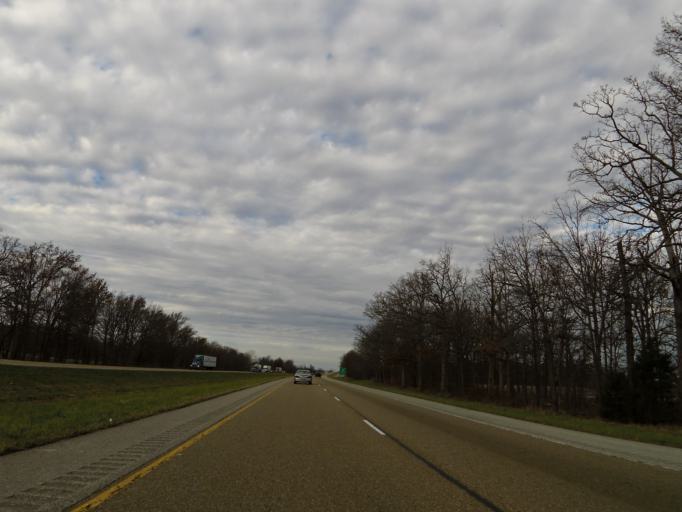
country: US
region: Illinois
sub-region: Clinton County
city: Wamac
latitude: 38.3878
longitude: -89.1541
